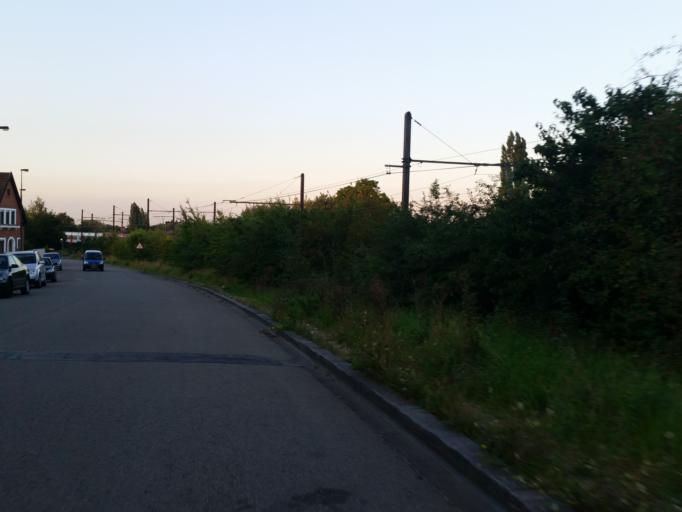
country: BE
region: Flanders
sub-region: Provincie Vlaams-Brabant
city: Diegem
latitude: 50.8935
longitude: 4.4234
